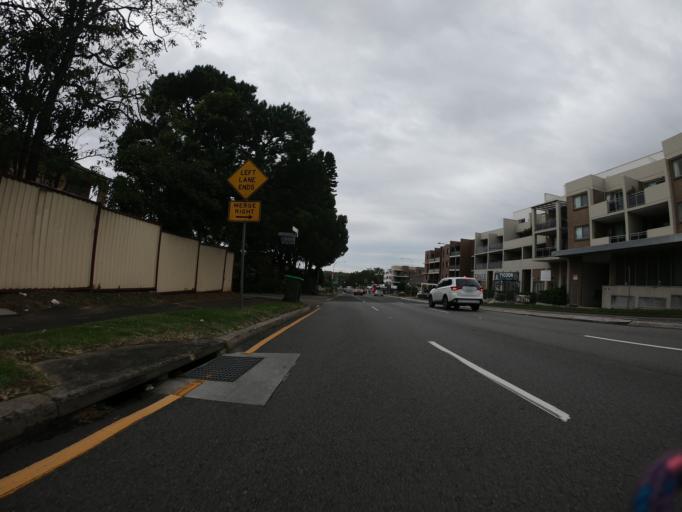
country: AU
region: New South Wales
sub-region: Parramatta
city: Harris Park
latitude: -33.8367
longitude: 151.0010
